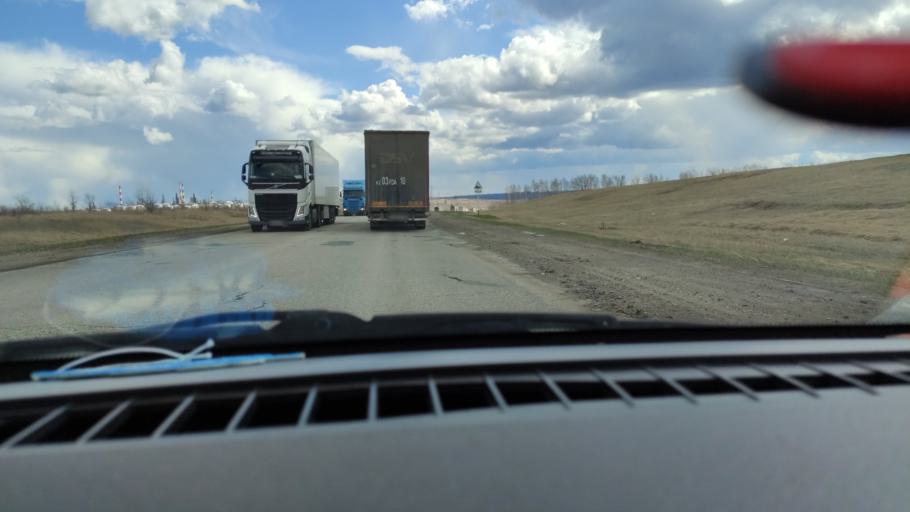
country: RU
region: Samara
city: Varlamovo
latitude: 53.1076
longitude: 48.3561
